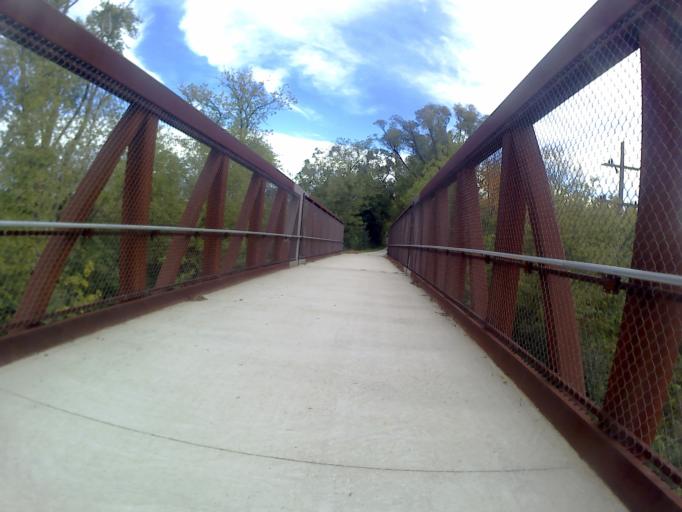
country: US
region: Illinois
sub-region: DuPage County
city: Wayne
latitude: 41.9473
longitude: -88.2373
